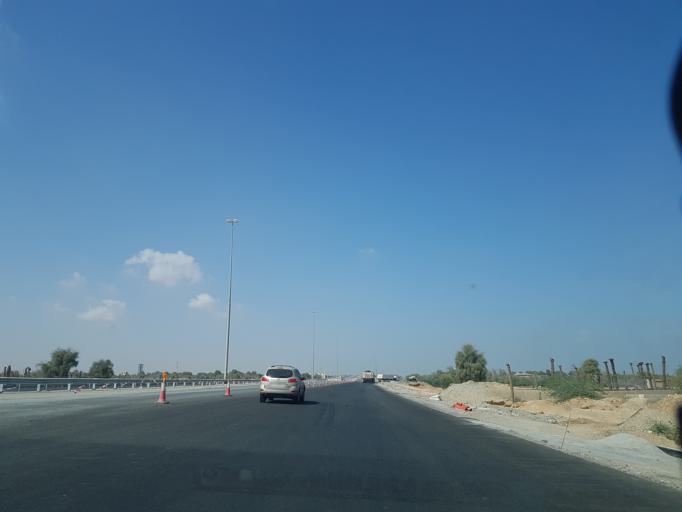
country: AE
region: Ra's al Khaymah
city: Ras al-Khaimah
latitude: 25.6978
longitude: 55.9756
